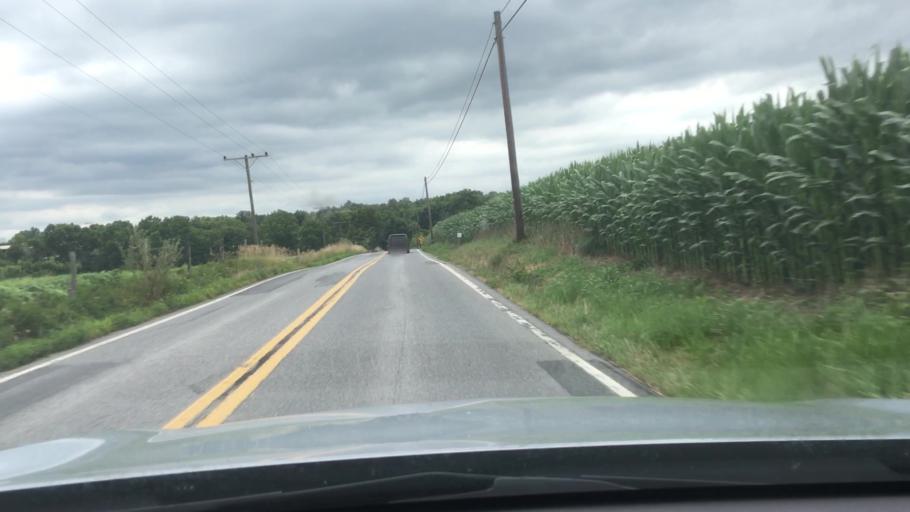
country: US
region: Pennsylvania
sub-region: Franklin County
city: Greencastle
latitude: 39.8645
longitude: -77.7921
